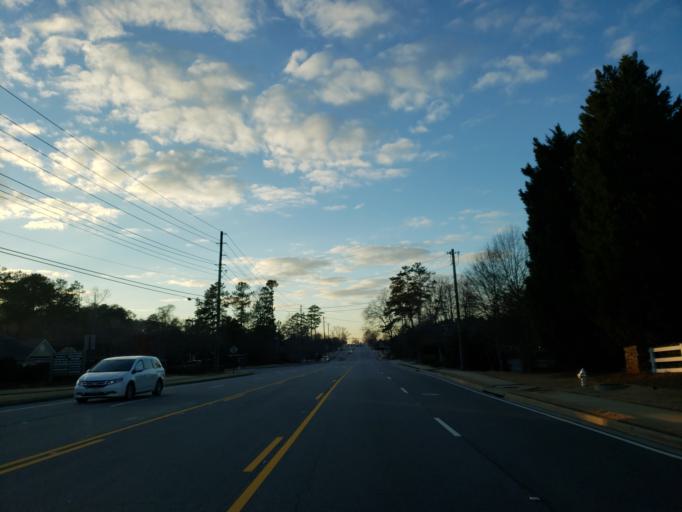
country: US
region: Georgia
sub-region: Cobb County
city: Acworth
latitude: 33.9950
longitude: -84.6990
